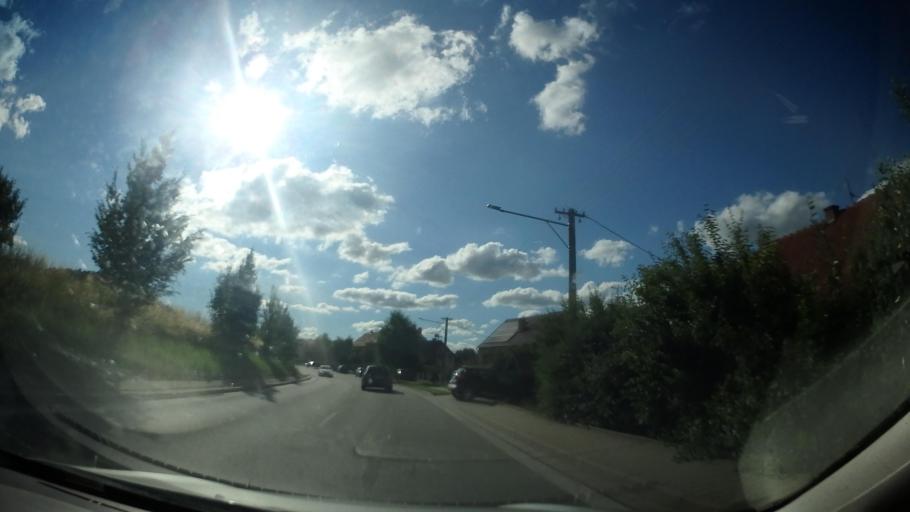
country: CZ
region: South Moravian
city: Boritov
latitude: 49.4190
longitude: 16.5933
